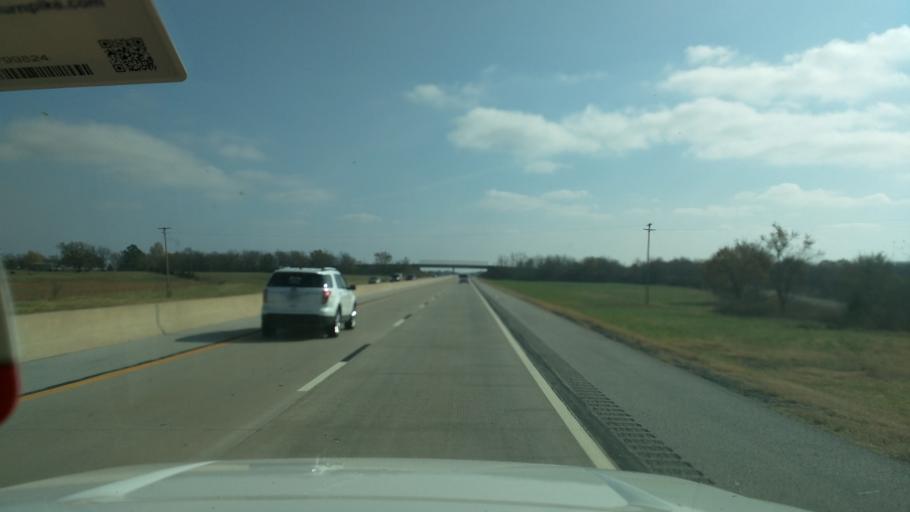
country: US
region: Oklahoma
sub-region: Wagoner County
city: Coweta
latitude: 35.9161
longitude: -95.5549
